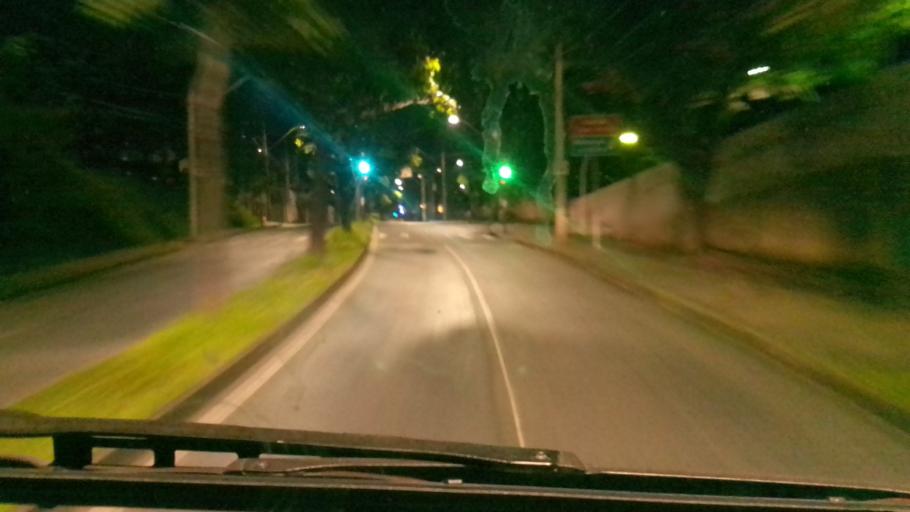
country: BR
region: Minas Gerais
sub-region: Belo Horizonte
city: Belo Horizonte
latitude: -19.9062
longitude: -43.9132
